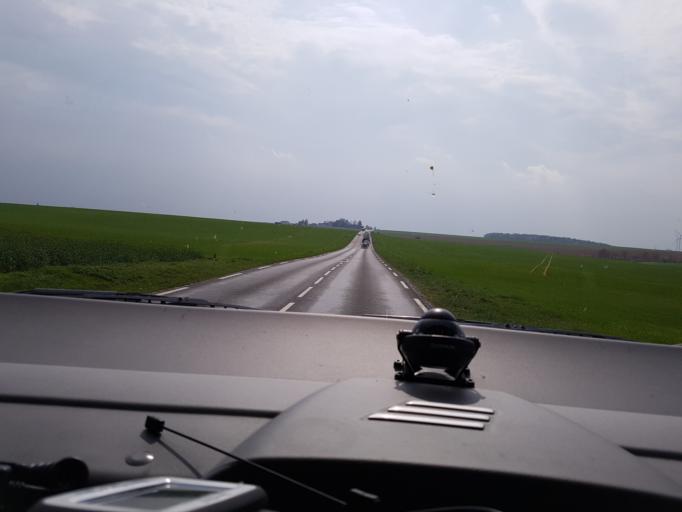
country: FR
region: Picardie
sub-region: Departement de l'Aisne
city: Crouy
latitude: 49.4571
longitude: 3.3529
